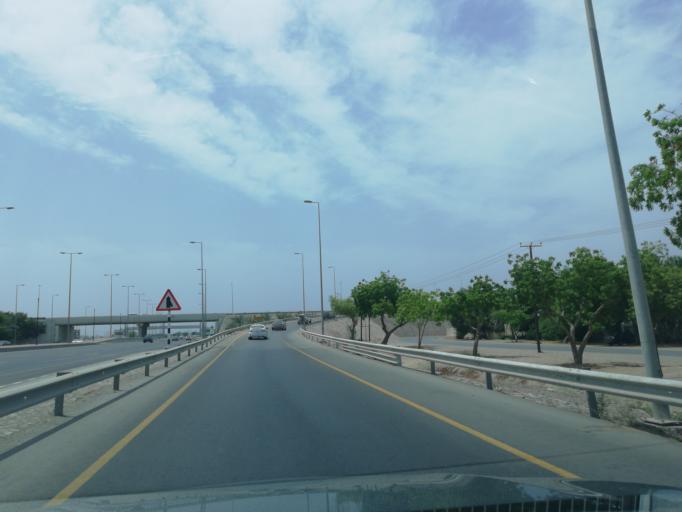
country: OM
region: Muhafazat Masqat
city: As Sib al Jadidah
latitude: 23.6742
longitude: 58.1401
